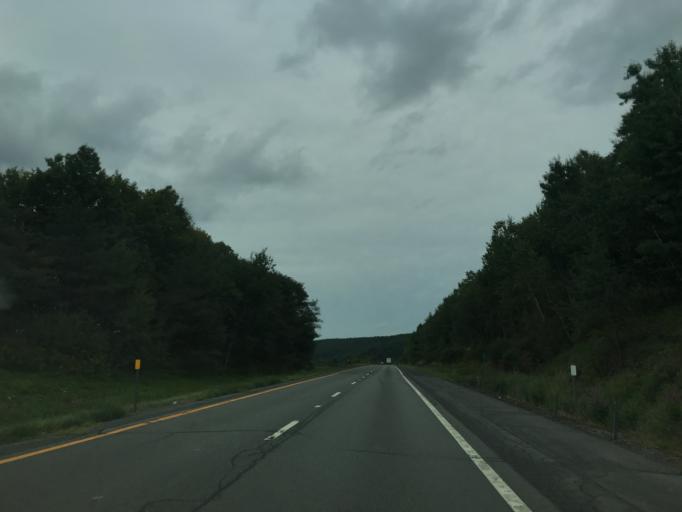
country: US
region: New York
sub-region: Chenango County
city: Bainbridge
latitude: 42.2936
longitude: -75.4561
